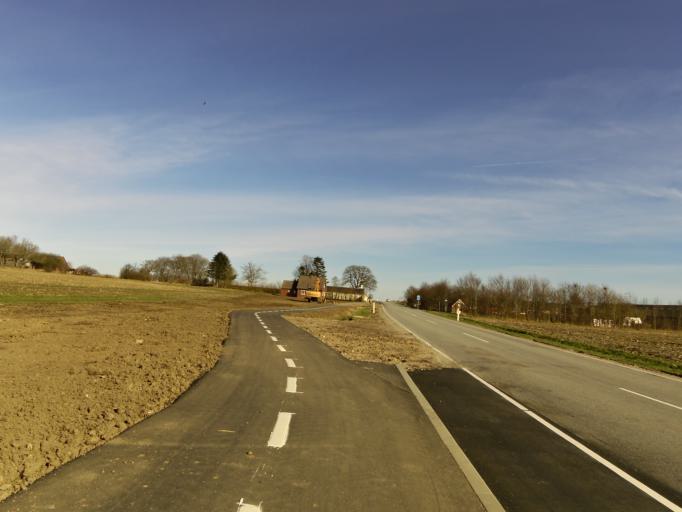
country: DK
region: South Denmark
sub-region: Vejen Kommune
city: Rodding
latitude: 55.3590
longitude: 9.1702
